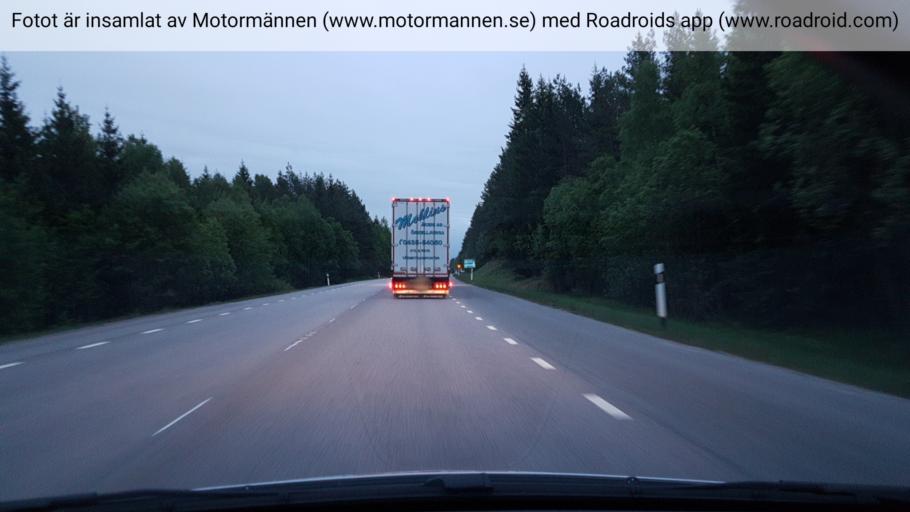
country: SE
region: Uppsala
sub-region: Heby Kommun
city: Heby
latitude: 59.9377
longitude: 16.8195
